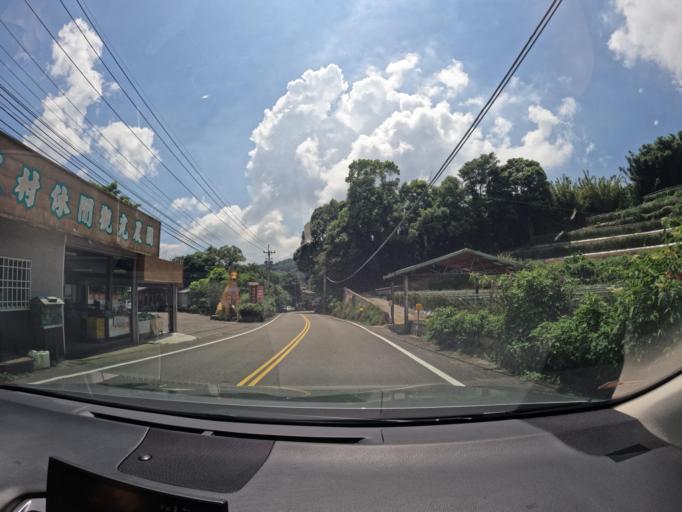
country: TW
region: Taiwan
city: Fengyuan
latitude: 24.3865
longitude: 120.8292
